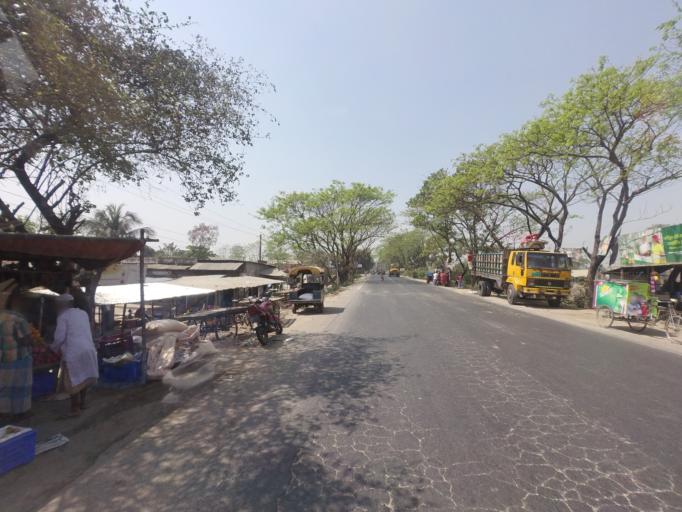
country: BD
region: Dhaka
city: Bhairab Bazar
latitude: 24.0436
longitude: 91.0581
